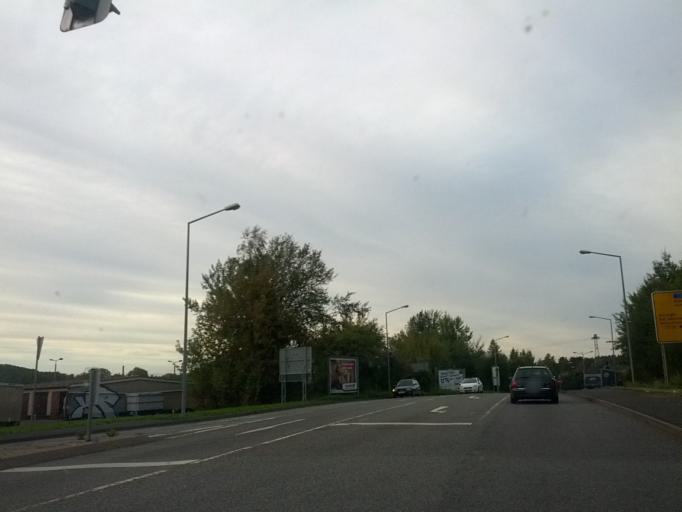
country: DE
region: Thuringia
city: Eisenach
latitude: 50.9949
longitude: 10.3168
